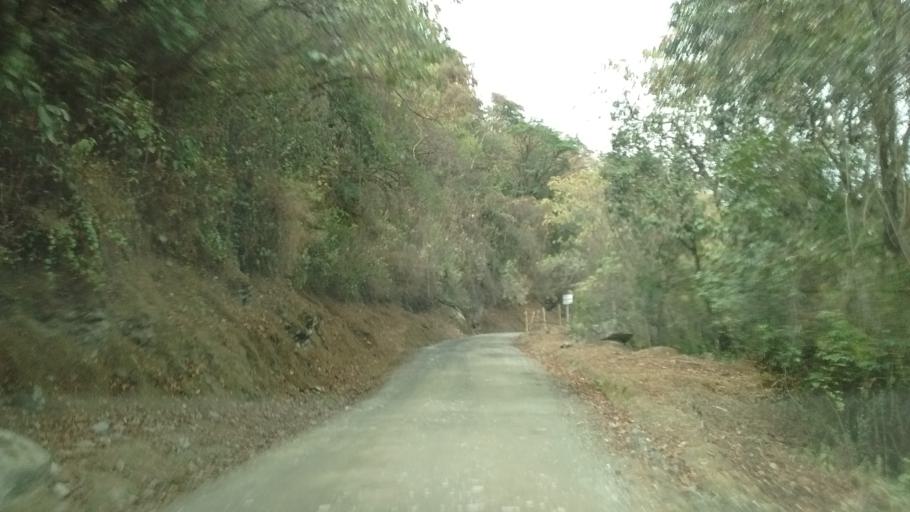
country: CO
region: Cauca
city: Almaguer
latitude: 1.8545
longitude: -76.9471
